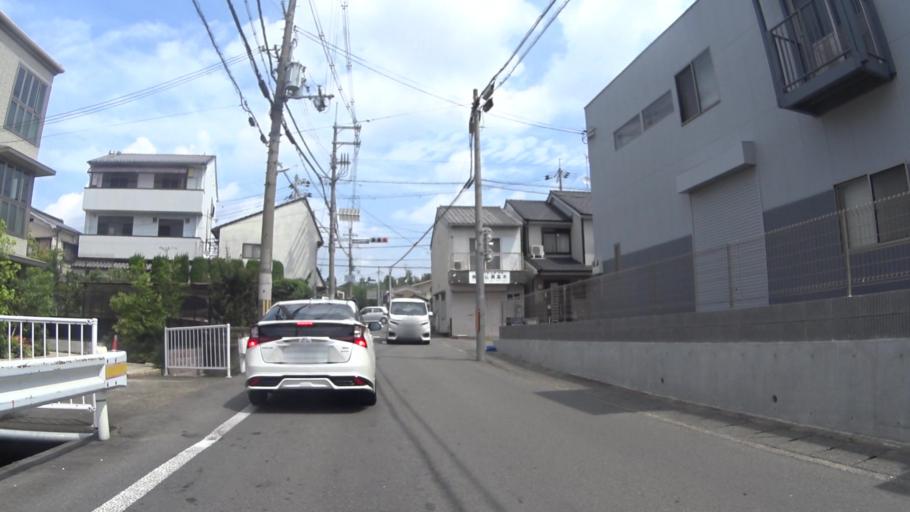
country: JP
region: Kyoto
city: Muko
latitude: 34.9451
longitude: 135.7335
